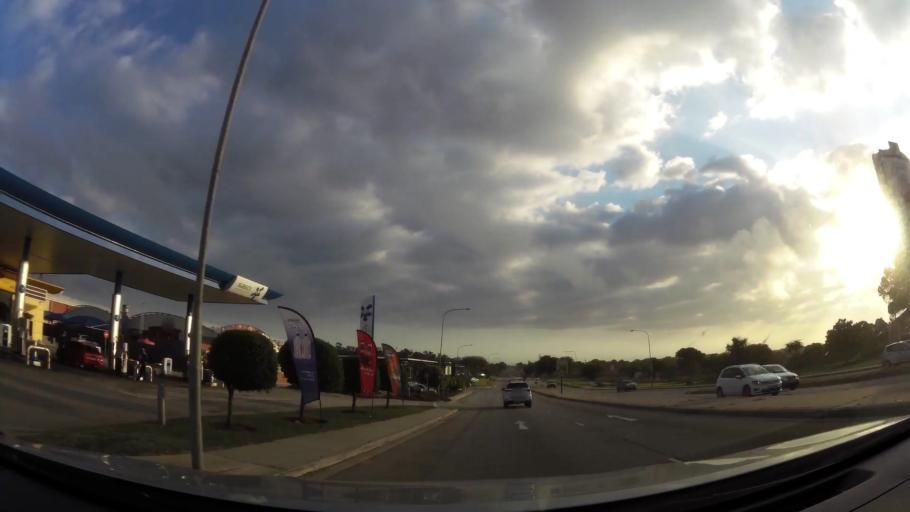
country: ZA
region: Eastern Cape
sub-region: Nelson Mandela Bay Metropolitan Municipality
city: Port Elizabeth
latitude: -33.9807
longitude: 25.5530
